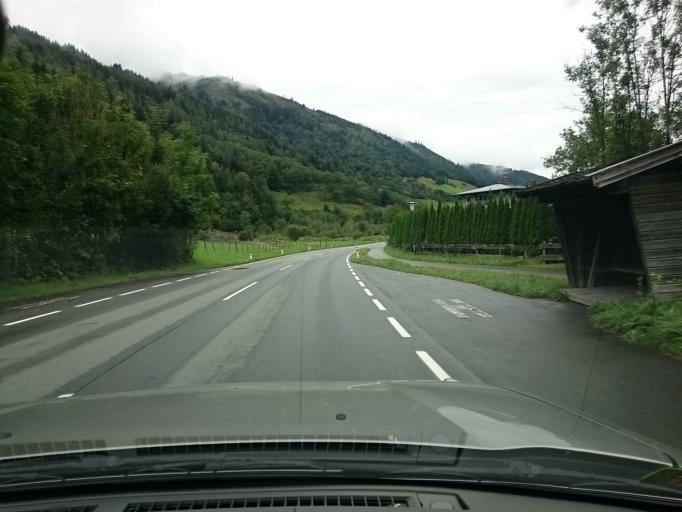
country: AT
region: Salzburg
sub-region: Politischer Bezirk Zell am See
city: Bruck an der Grossglocknerstrasse
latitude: 47.2368
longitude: 12.8255
